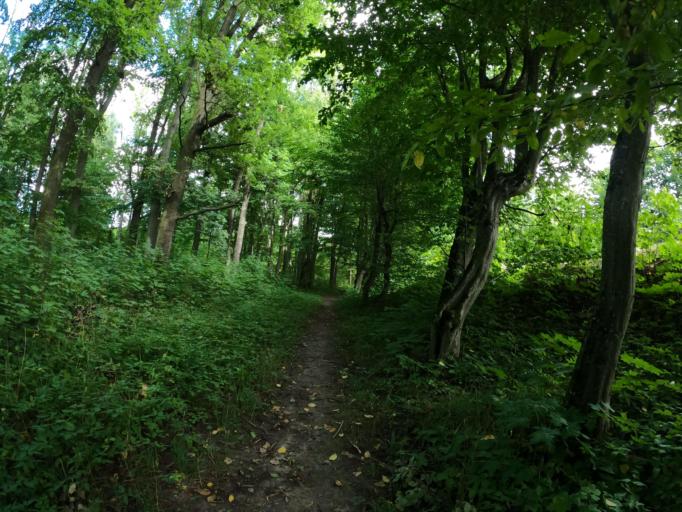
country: RU
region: Kaliningrad
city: Zheleznodorozhnyy
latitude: 54.3542
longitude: 21.3119
